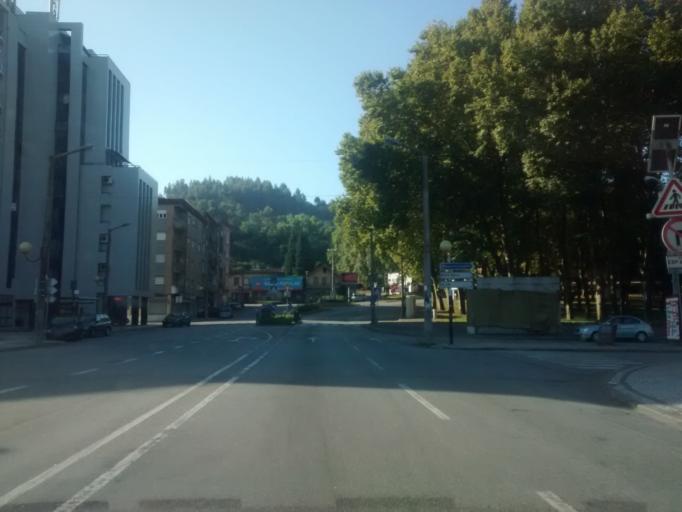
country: PT
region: Braga
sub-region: Braga
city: Braga
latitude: 41.5432
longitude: -8.4183
